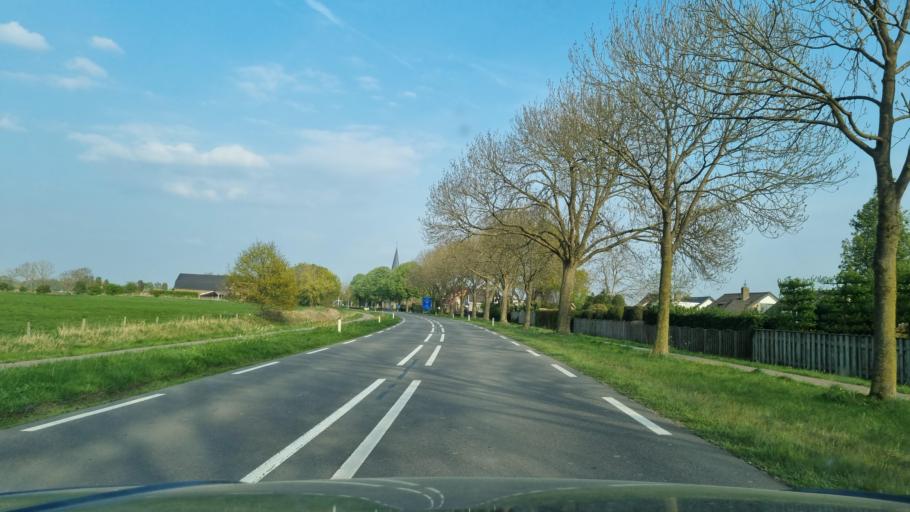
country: NL
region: North Brabant
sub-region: Gemeente Cuijk
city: Cuijk
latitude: 51.7270
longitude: 5.8198
